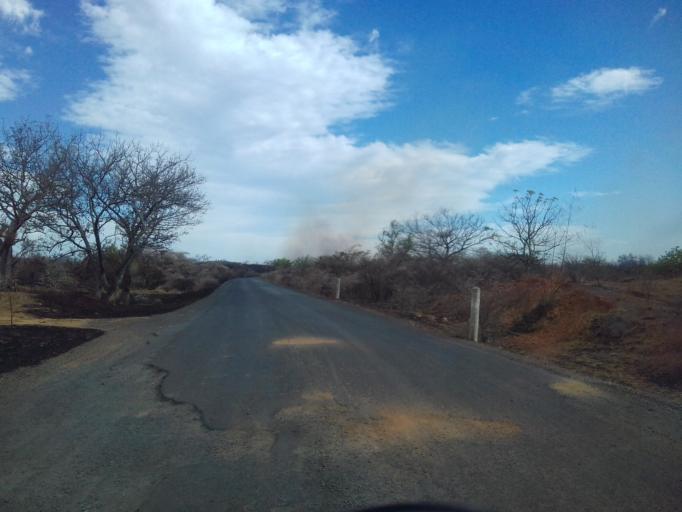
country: MG
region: Sofia
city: Antsohihy
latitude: -15.1913
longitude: 47.8358
